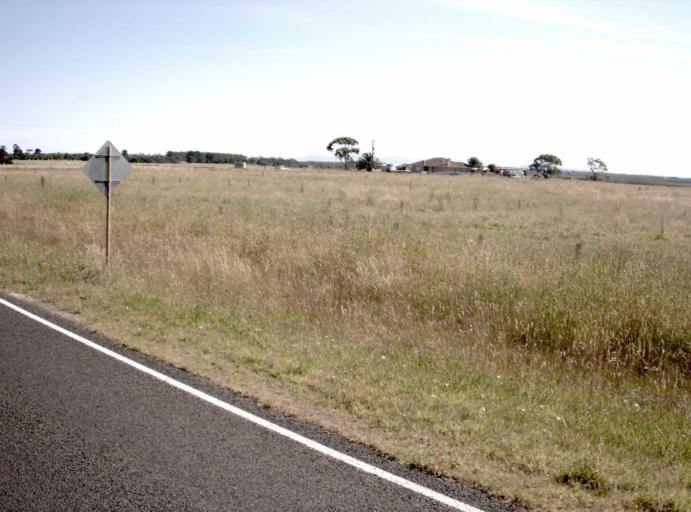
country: AU
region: Victoria
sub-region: Latrobe
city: Traralgon
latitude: -38.6232
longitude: 146.6733
